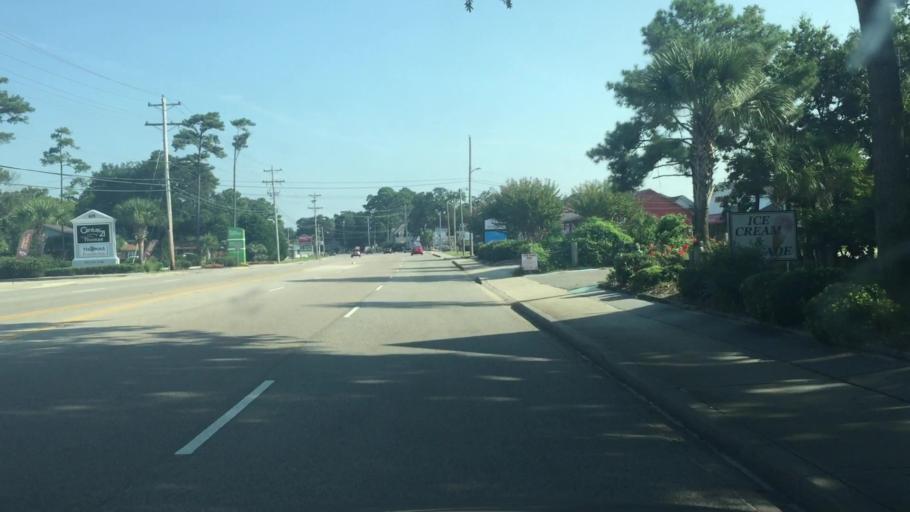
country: US
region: South Carolina
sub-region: Horry County
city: North Myrtle Beach
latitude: 33.8347
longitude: -78.6446
